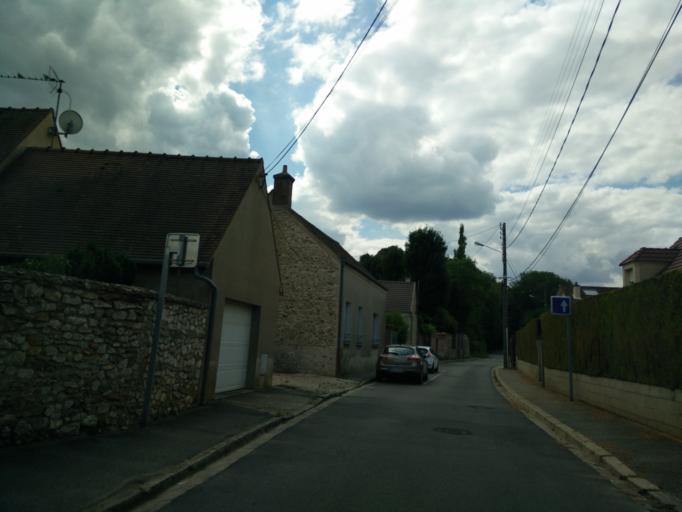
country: FR
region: Ile-de-France
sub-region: Departement des Yvelines
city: Garancieres
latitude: 48.8196
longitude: 1.7537
